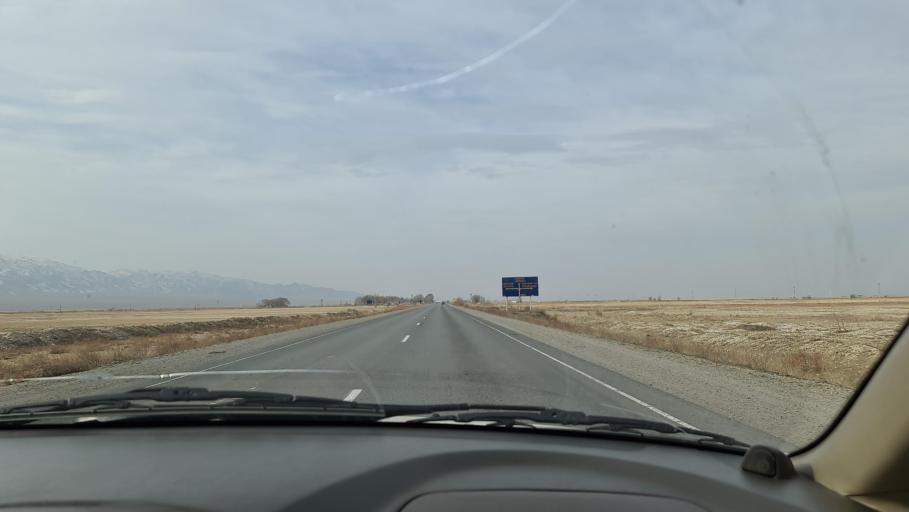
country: KG
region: Chuy
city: Tokmok
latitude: 43.3487
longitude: 75.4894
